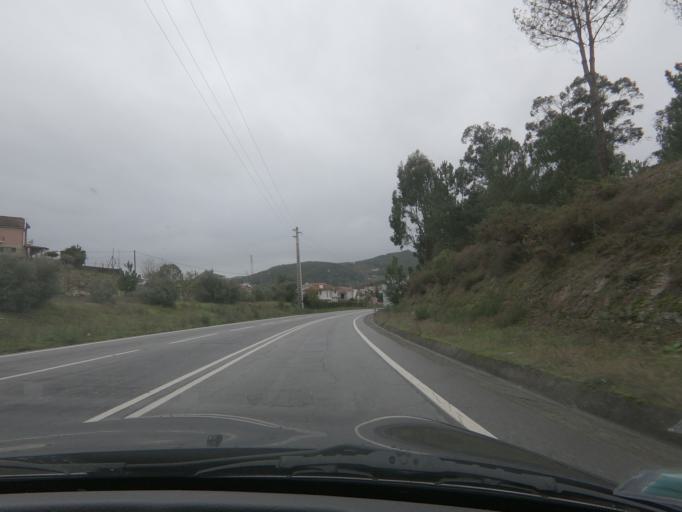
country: PT
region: Porto
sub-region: Amarante
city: Teloes
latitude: 41.2948
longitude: -8.0949
